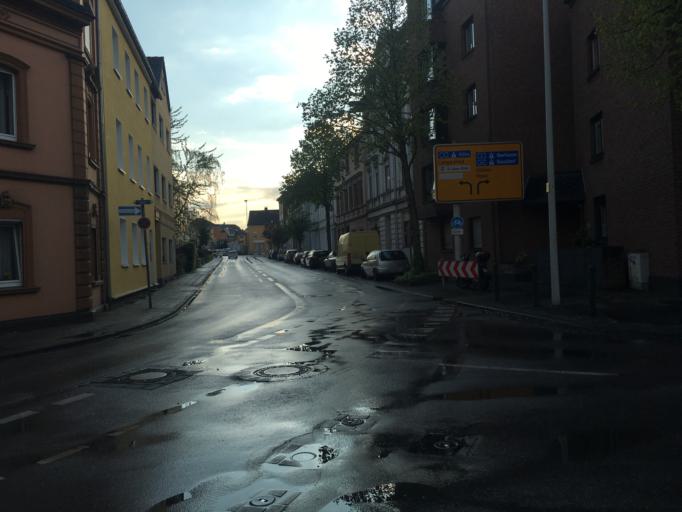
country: DE
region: North Rhine-Westphalia
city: Haan
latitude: 51.1610
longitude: 6.9964
